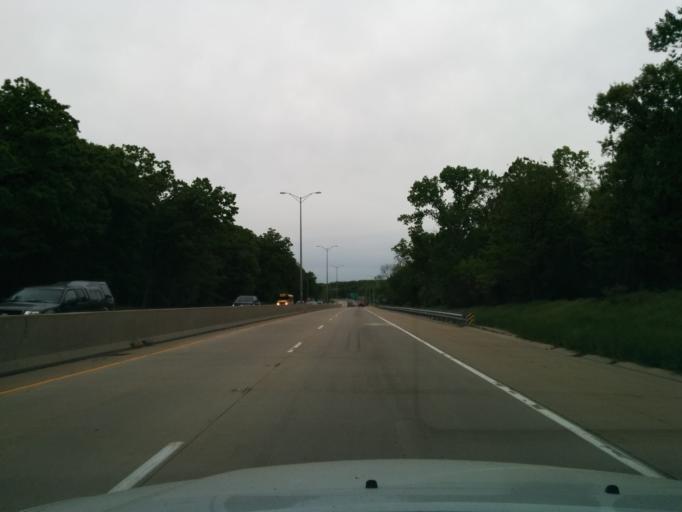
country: US
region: Illinois
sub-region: Cook County
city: Willow Springs
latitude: 41.7284
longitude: -87.8522
